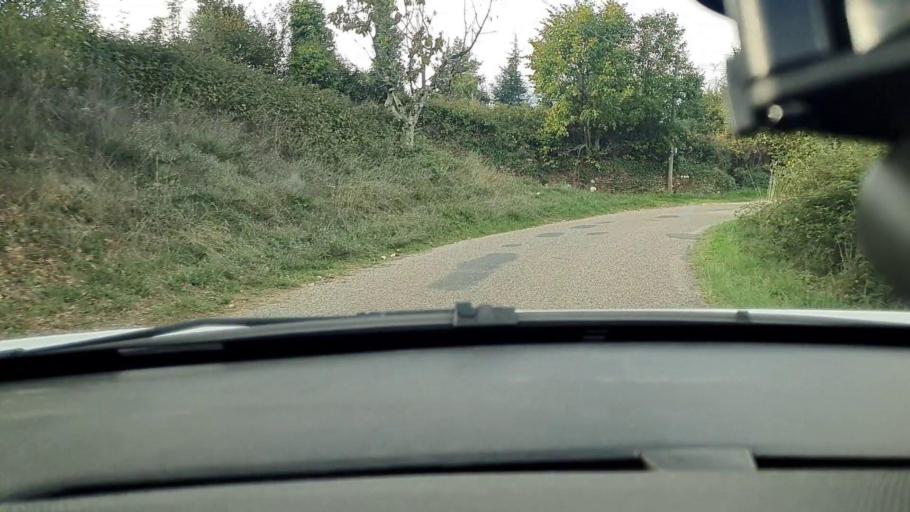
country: FR
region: Languedoc-Roussillon
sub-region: Departement du Gard
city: Besseges
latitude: 44.3240
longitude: 4.0325
